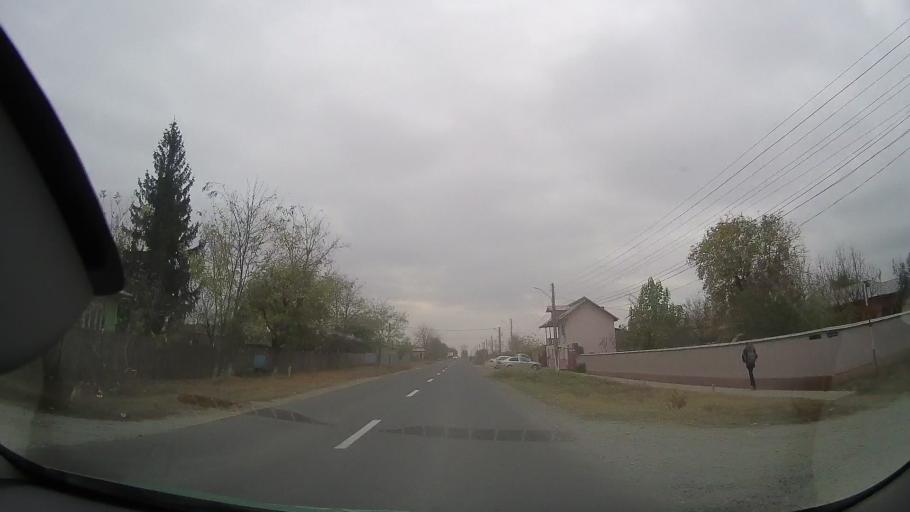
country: RO
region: Ialomita
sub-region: Comuna Garbovi
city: Garbovi
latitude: 44.7811
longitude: 26.7555
